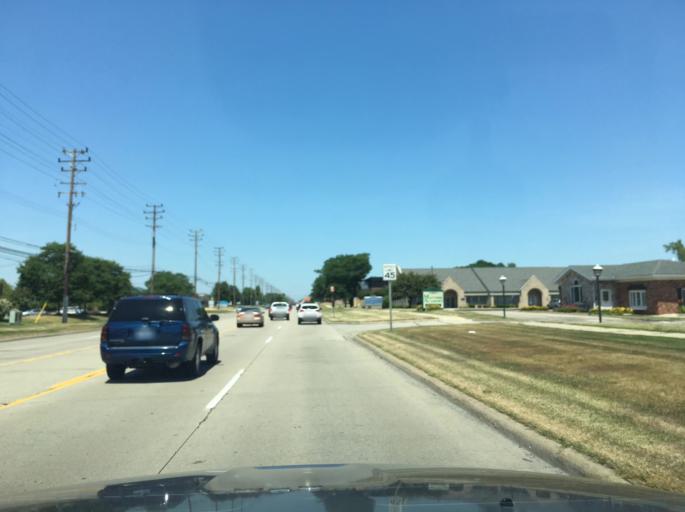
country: US
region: Michigan
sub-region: Macomb County
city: Clinton
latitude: 42.5844
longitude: -82.9518
